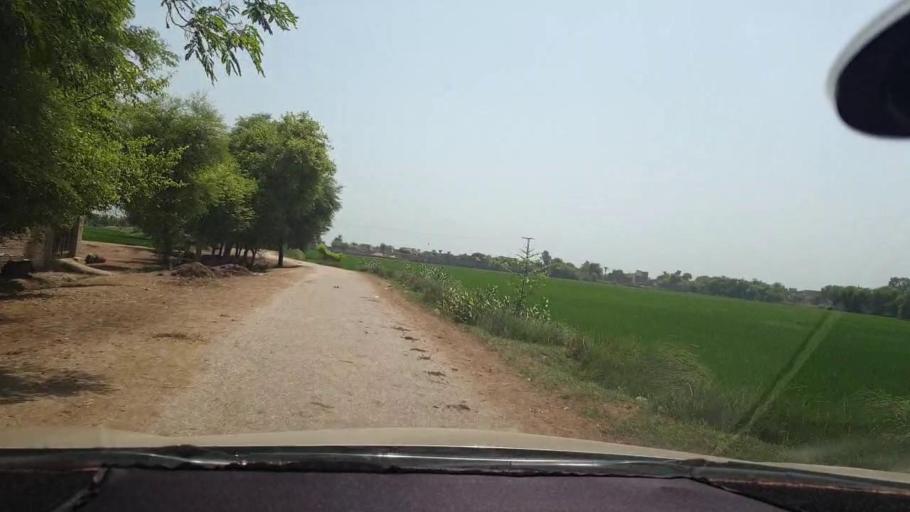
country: PK
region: Sindh
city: Kambar
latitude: 27.6779
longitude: 67.9408
